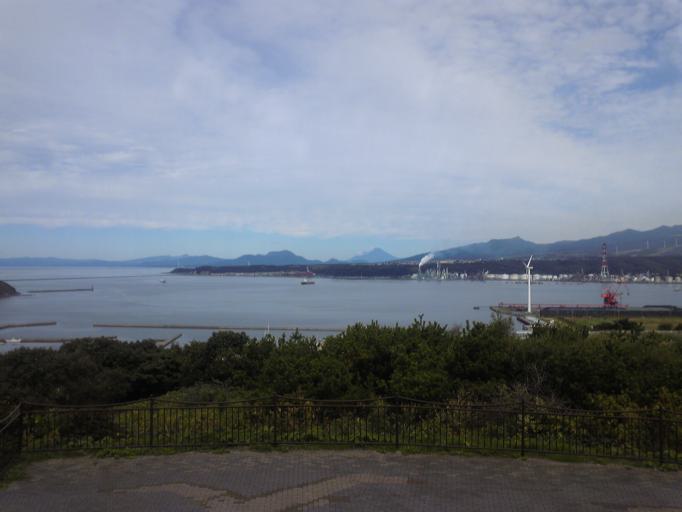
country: JP
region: Hokkaido
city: Muroran
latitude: 42.3367
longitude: 140.9420
